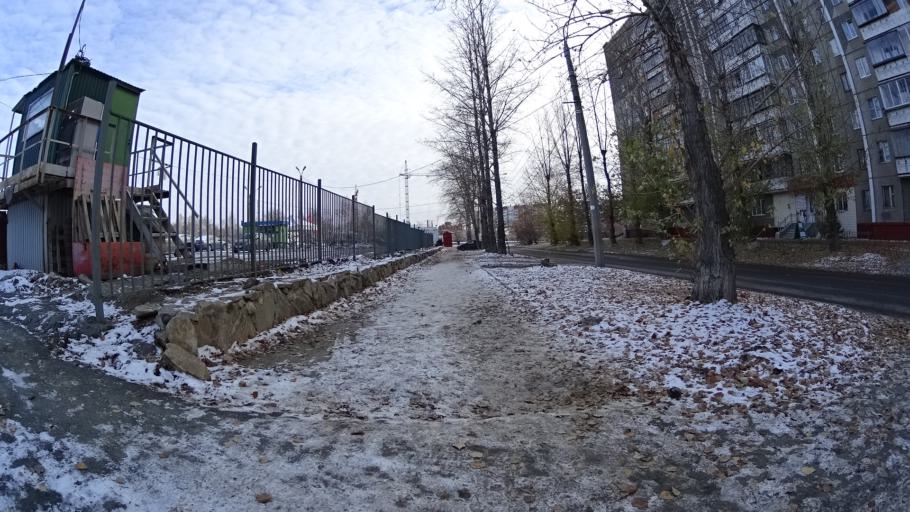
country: RU
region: Chelyabinsk
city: Roshchino
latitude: 55.1886
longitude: 61.3024
